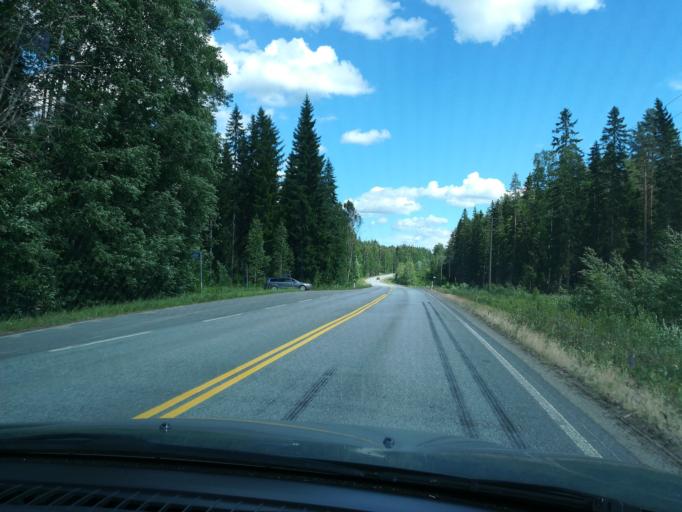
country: FI
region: Southern Savonia
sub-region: Mikkeli
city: Hirvensalmi
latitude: 61.6554
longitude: 27.0039
